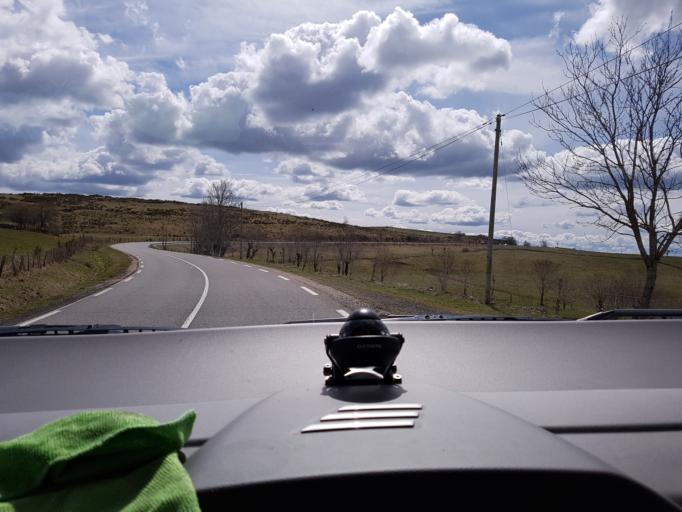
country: FR
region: Midi-Pyrenees
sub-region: Departement de l'Aveyron
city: Laguiole
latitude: 44.7191
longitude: 2.8671
